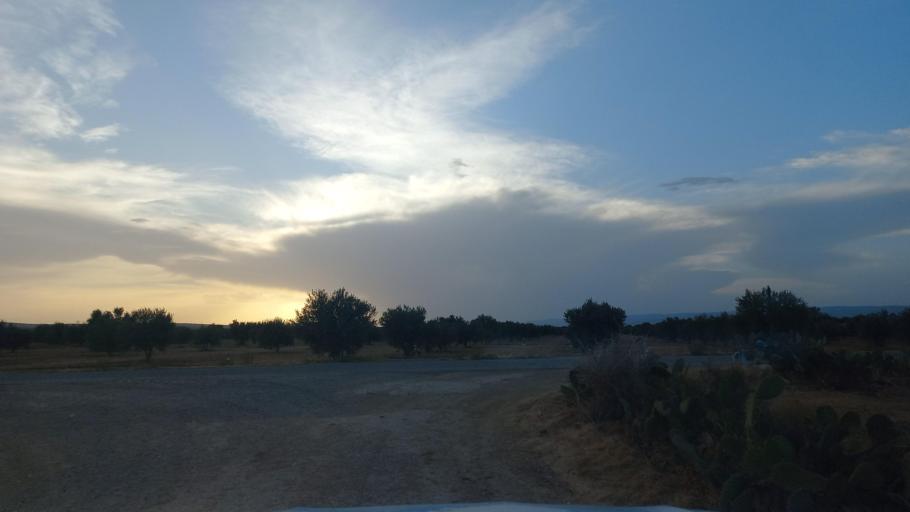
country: TN
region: Al Qasrayn
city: Kasserine
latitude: 35.2119
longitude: 9.0424
